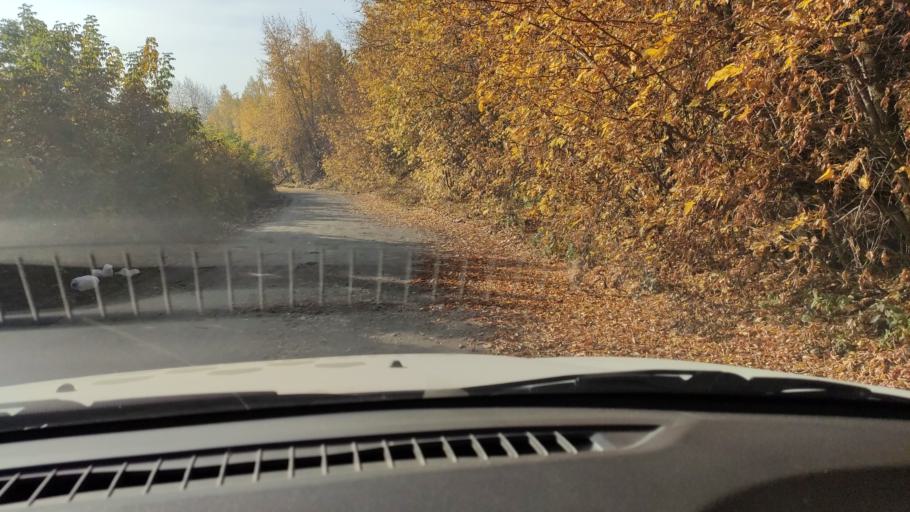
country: RU
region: Perm
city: Kondratovo
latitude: 58.0084
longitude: 56.1574
